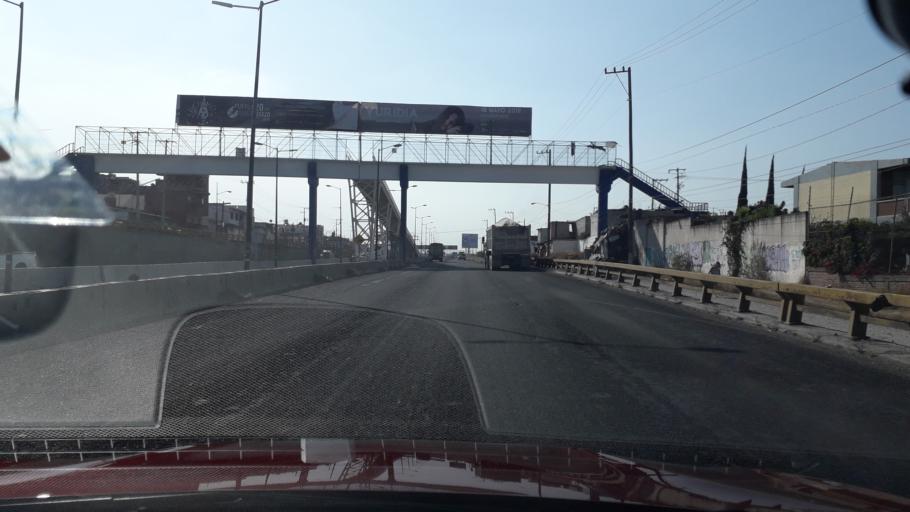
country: MX
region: Puebla
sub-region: Puebla
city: El Capulo (La Quebradora)
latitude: 18.9820
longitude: -98.2259
